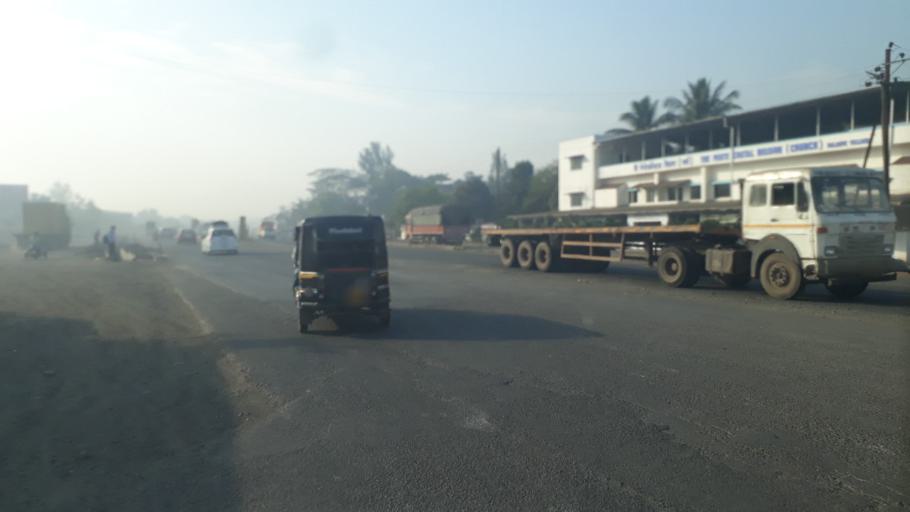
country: IN
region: Maharashtra
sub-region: Raigarh
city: Kalundri
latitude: 18.9573
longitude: 73.1309
